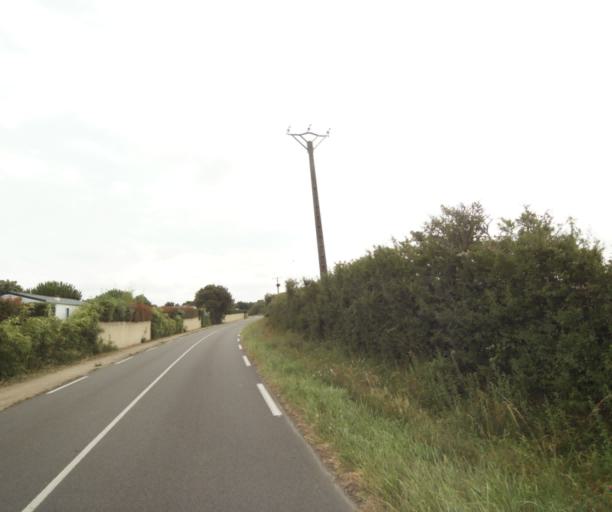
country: FR
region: Pays de la Loire
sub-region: Departement de la Vendee
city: Chateau-d'Olonne
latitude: 46.4715
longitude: -1.7245
